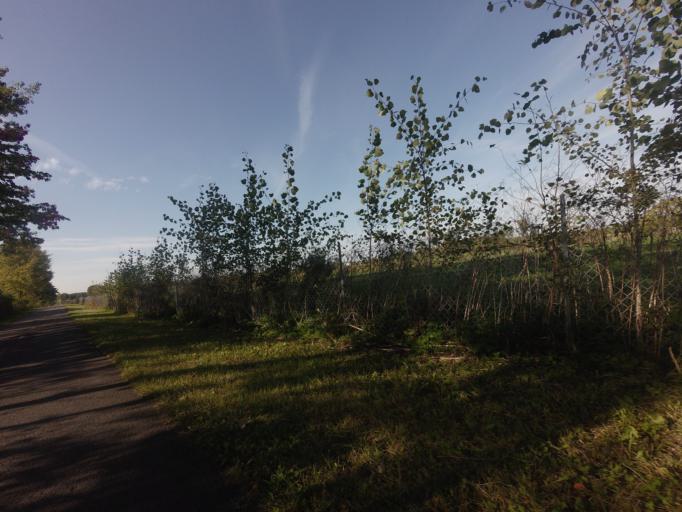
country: CA
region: Quebec
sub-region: Laurentides
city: Blainville
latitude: 45.7189
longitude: -73.9278
